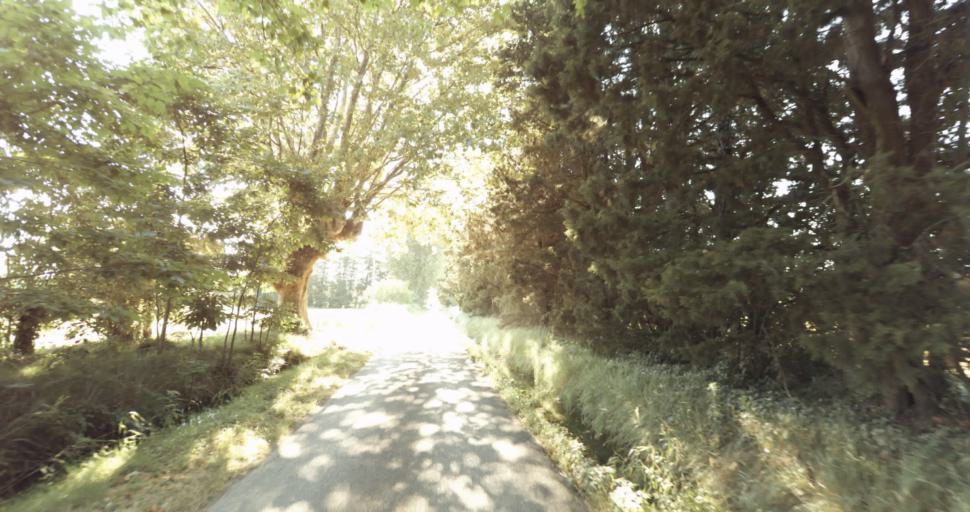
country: FR
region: Provence-Alpes-Cote d'Azur
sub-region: Departement du Vaucluse
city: Monteux
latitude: 44.0435
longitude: 4.9609
